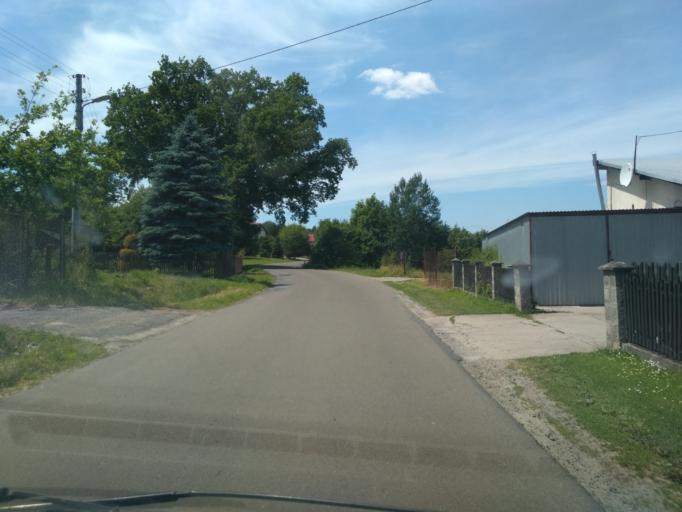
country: PL
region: Subcarpathian Voivodeship
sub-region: Powiat strzyzowski
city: Strzyzow
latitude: 49.8629
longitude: 21.7719
